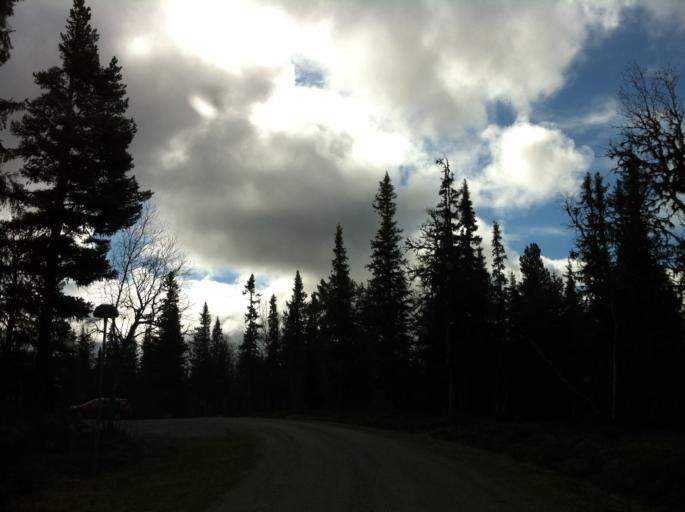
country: NO
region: Hedmark
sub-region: Engerdal
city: Engerdal
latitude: 62.5412
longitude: 12.4449
